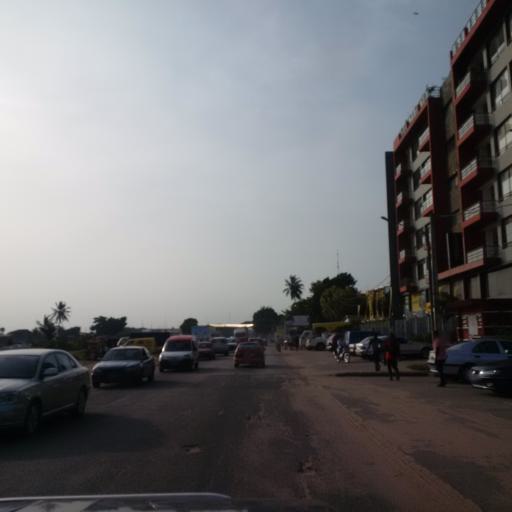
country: CI
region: Lagunes
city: Abidjan
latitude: 5.2881
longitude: -3.9880
